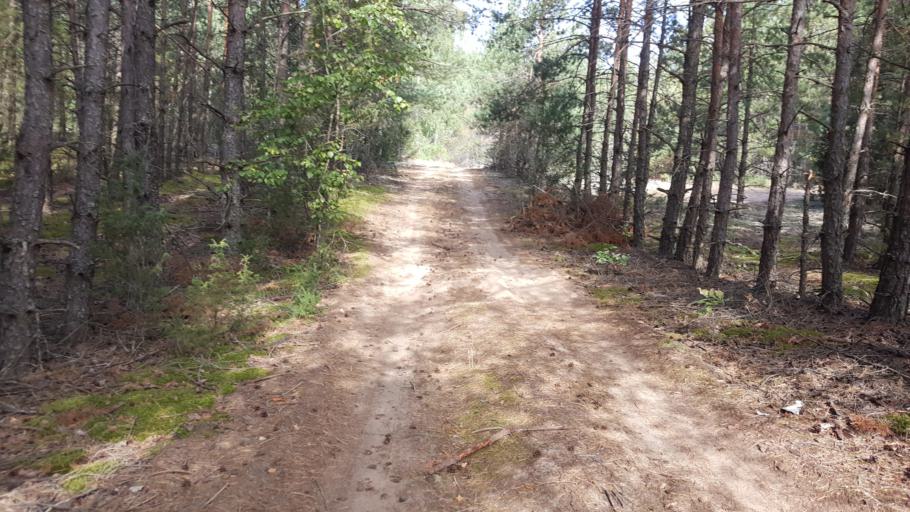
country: BY
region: Brest
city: Ivatsevichy
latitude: 52.7950
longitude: 25.5592
